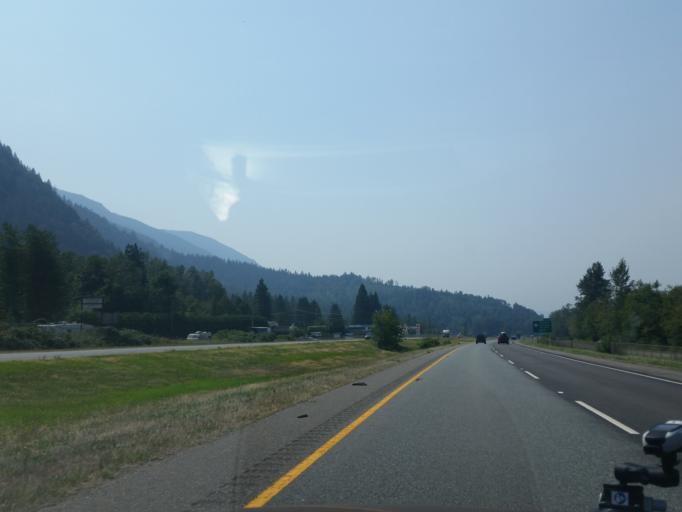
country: CA
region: British Columbia
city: Agassiz
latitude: 49.1887
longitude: -121.7438
